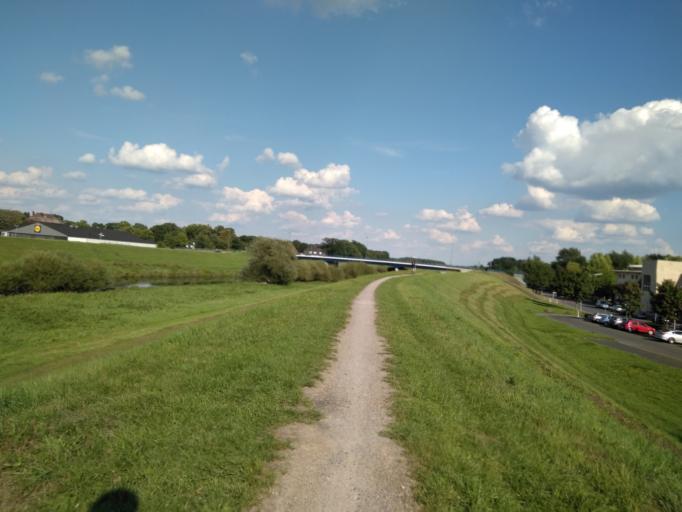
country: DE
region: North Rhine-Westphalia
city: Dorsten
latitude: 51.6679
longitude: 6.9624
